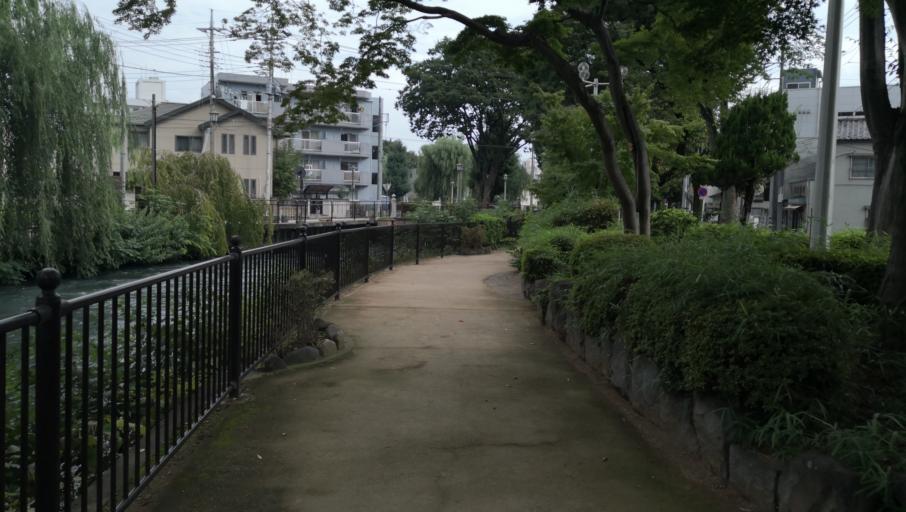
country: JP
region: Gunma
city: Maebashi-shi
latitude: 36.3962
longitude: 139.0664
